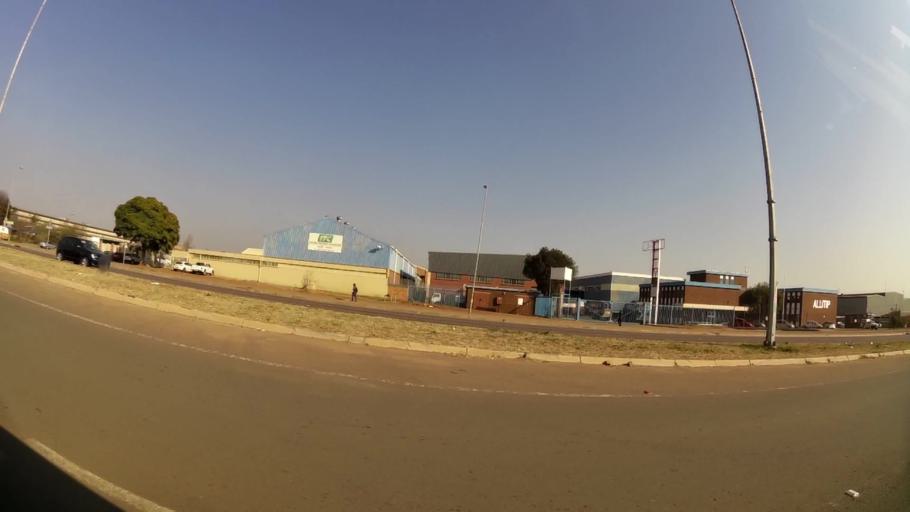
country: ZA
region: Gauteng
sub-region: City of Tshwane Metropolitan Municipality
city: Pretoria
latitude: -25.7265
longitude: 28.3324
